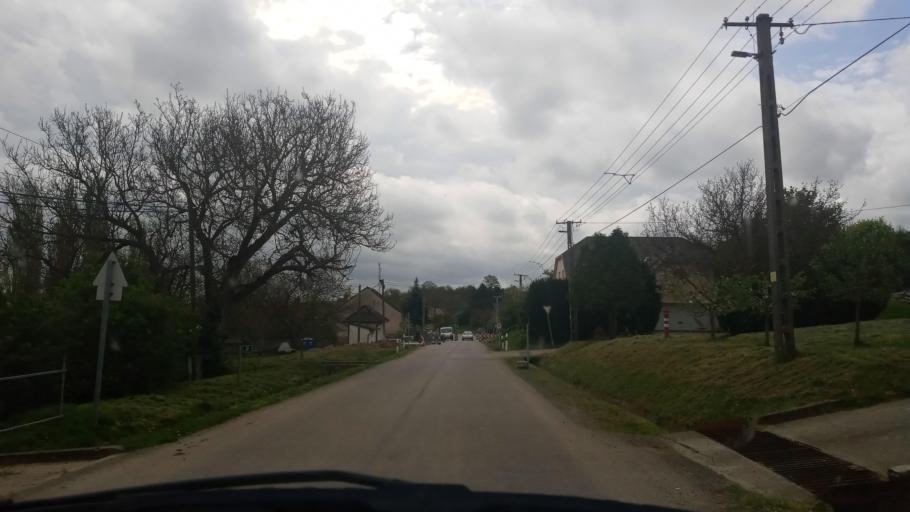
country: HU
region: Baranya
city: Boly
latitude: 45.9782
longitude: 18.4244
